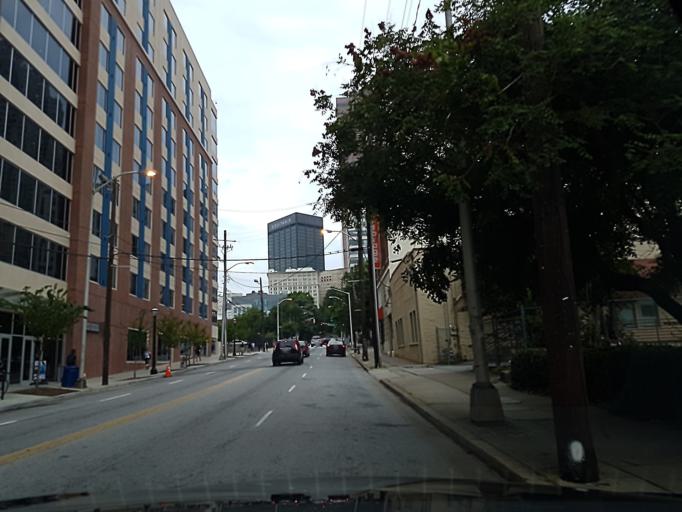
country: US
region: Georgia
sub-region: Fulton County
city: Atlanta
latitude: 33.7572
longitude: -84.3827
